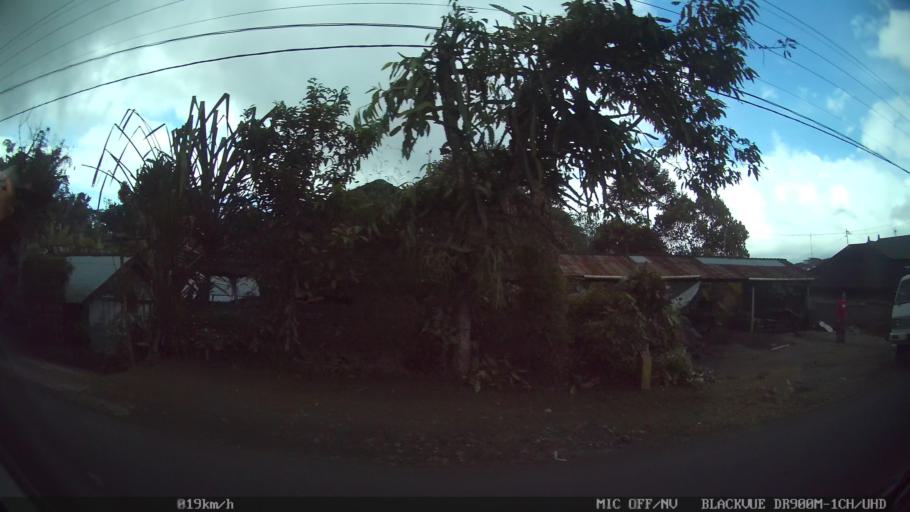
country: ID
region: Bali
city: Banjar Bias
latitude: -8.3126
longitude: 115.3999
